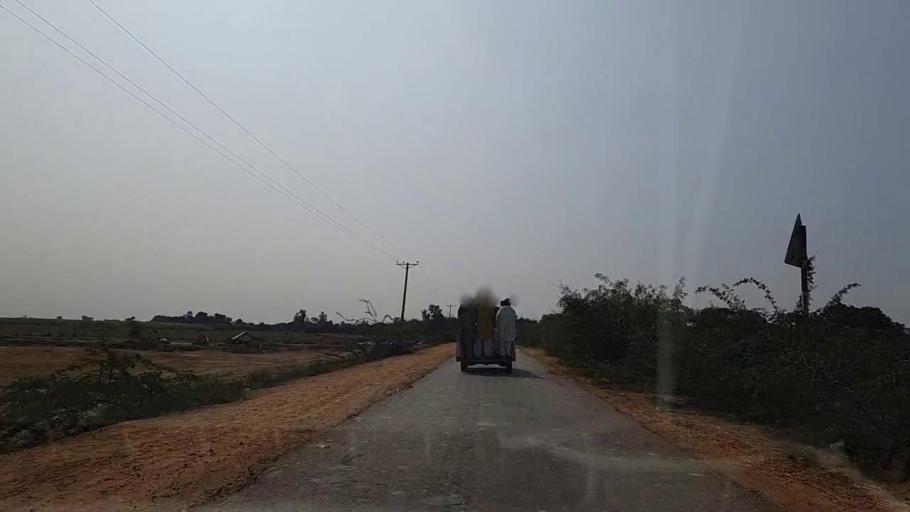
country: PK
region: Sindh
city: Chuhar Jamali
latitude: 24.3726
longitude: 67.9673
